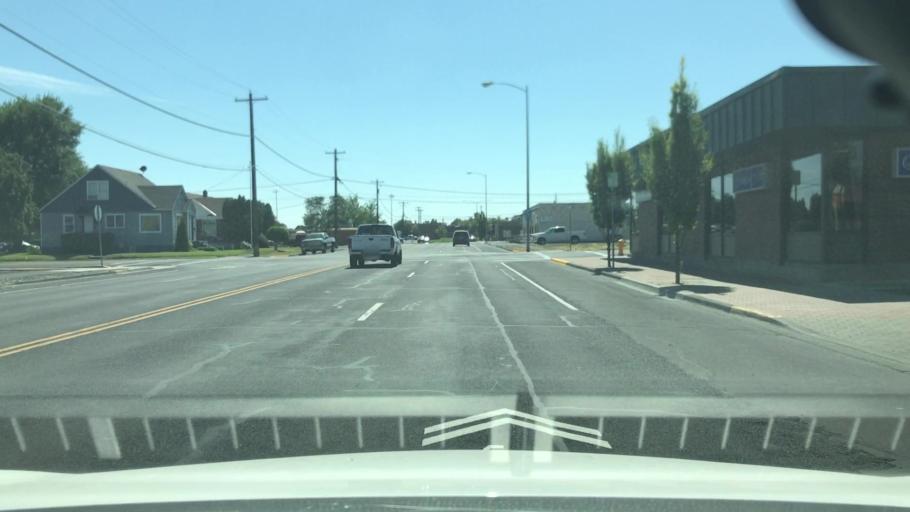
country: US
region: Washington
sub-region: Grant County
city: Moses Lake
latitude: 47.1284
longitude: -119.2792
